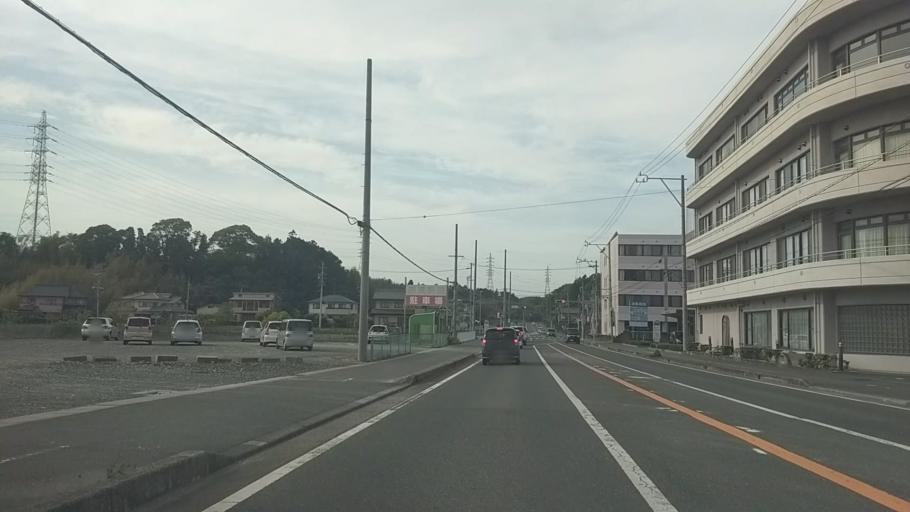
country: JP
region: Shizuoka
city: Hamamatsu
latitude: 34.7459
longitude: 137.6547
